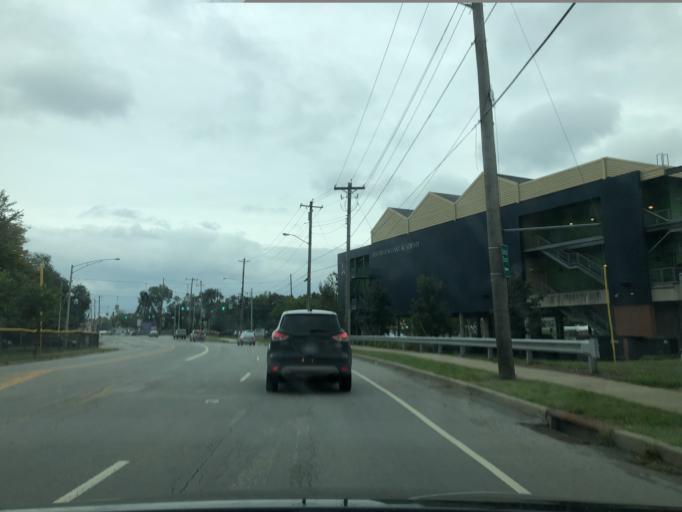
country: US
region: Kentucky
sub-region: Campbell County
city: Dayton
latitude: 39.1144
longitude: -84.4405
